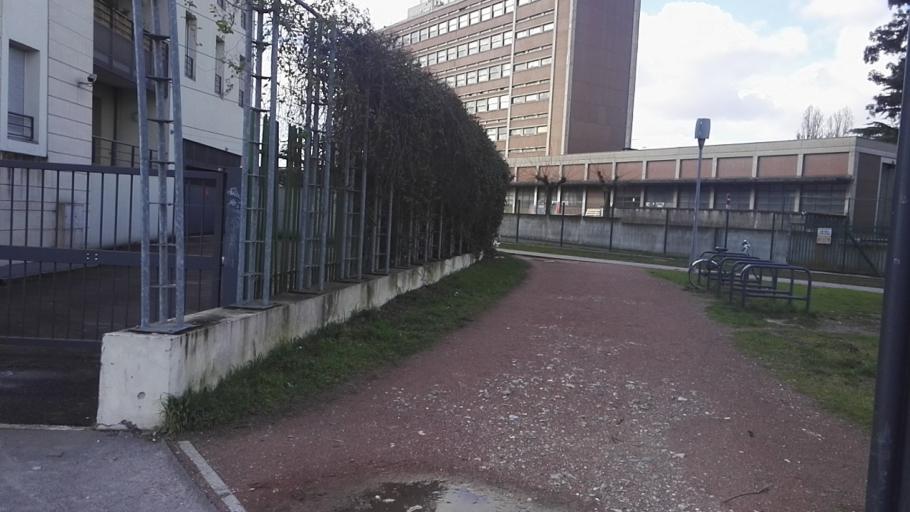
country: FR
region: Aquitaine
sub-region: Departement de la Gironde
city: Talence
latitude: 44.8076
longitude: -0.5915
